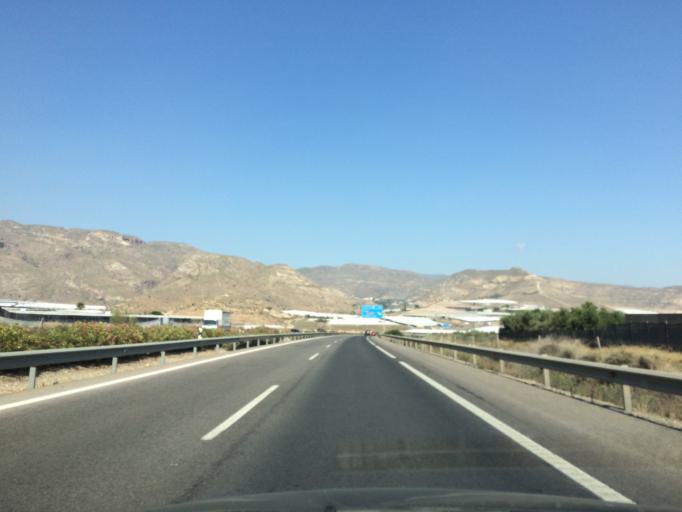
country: ES
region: Andalusia
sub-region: Provincia de Almeria
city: Vicar
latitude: 36.8078
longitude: -2.6689
